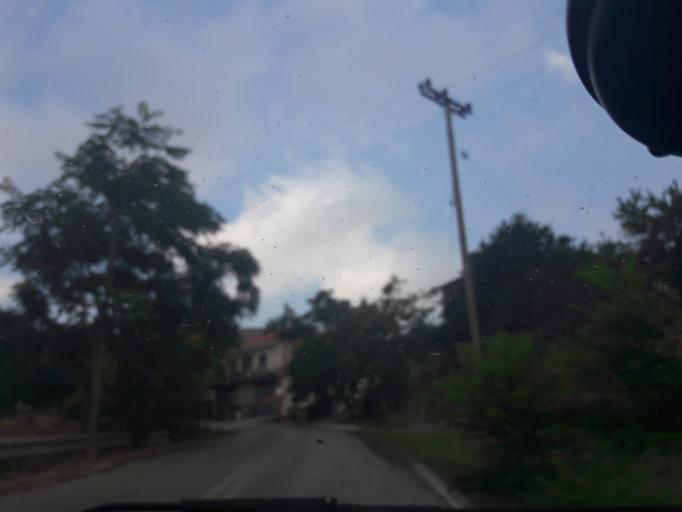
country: GR
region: North Aegean
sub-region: Nomos Lesvou
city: Myrina
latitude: 39.9487
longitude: 25.1660
